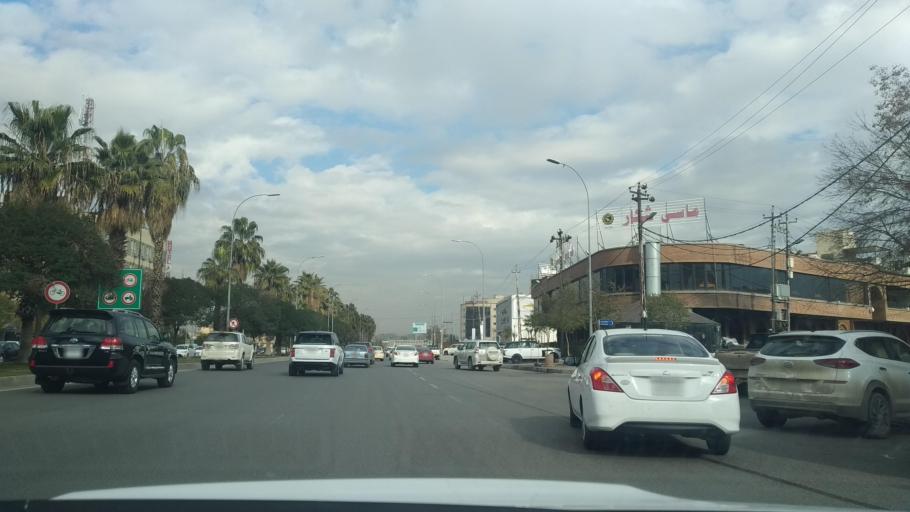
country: IQ
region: Arbil
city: Erbil
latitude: 36.1861
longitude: 43.9940
